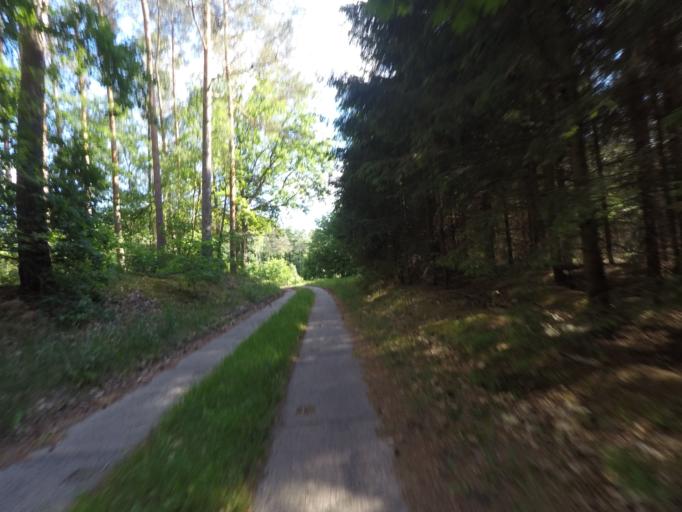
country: DE
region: Brandenburg
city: Britz
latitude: 52.8667
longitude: 13.7822
